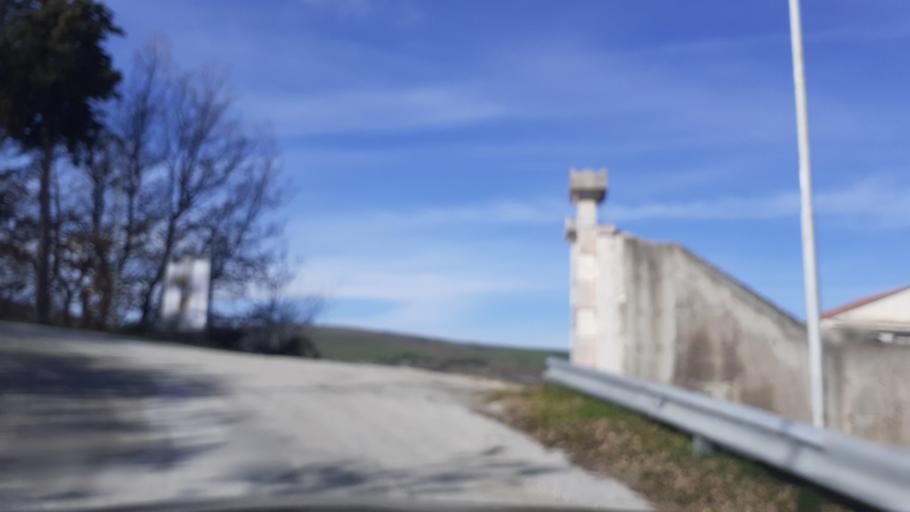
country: IT
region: Molise
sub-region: Provincia di Campobasso
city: Pietracupa
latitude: 41.6847
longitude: 14.5226
